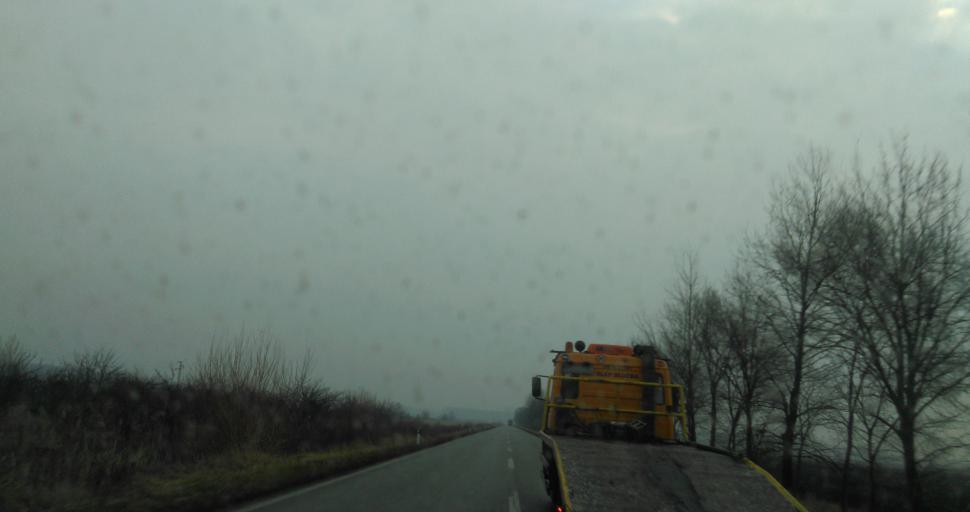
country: RS
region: Autonomna Pokrajina Vojvodina
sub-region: Srednjebanatski Okrug
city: Novi Becej
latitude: 45.5829
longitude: 20.0916
